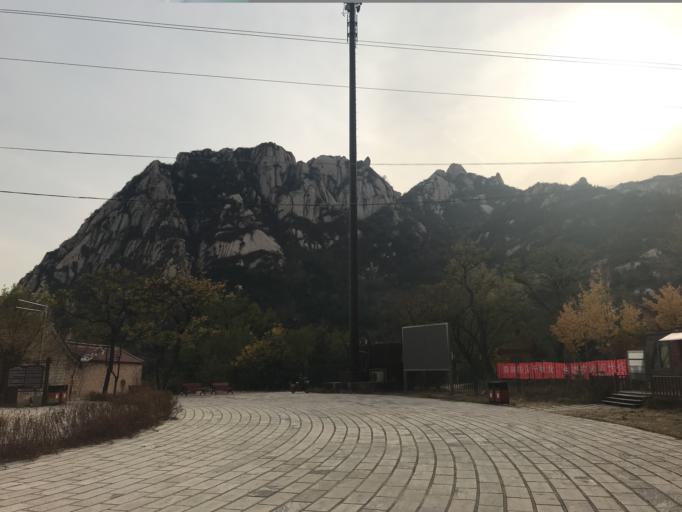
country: CN
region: Beijing
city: Yangfang
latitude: 40.1240
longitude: 116.0901
